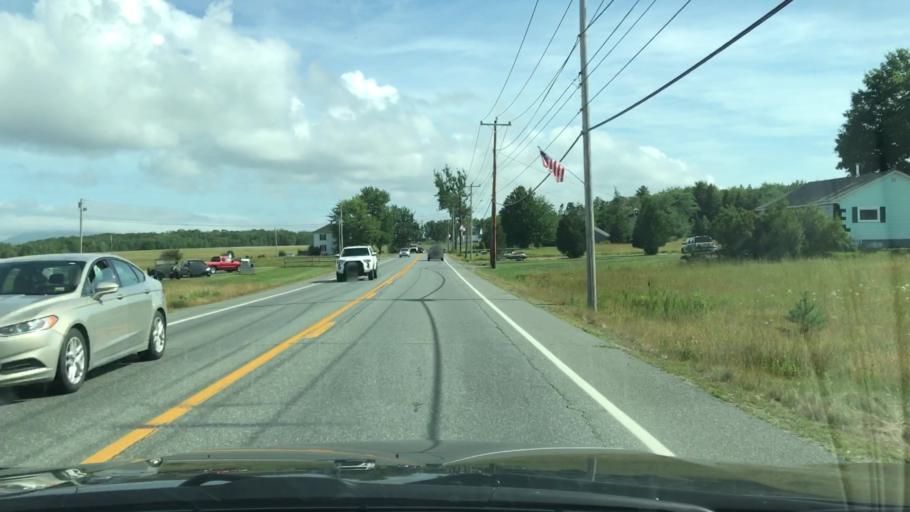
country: US
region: Maine
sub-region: Hancock County
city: Trenton
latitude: 44.4619
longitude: -68.3616
